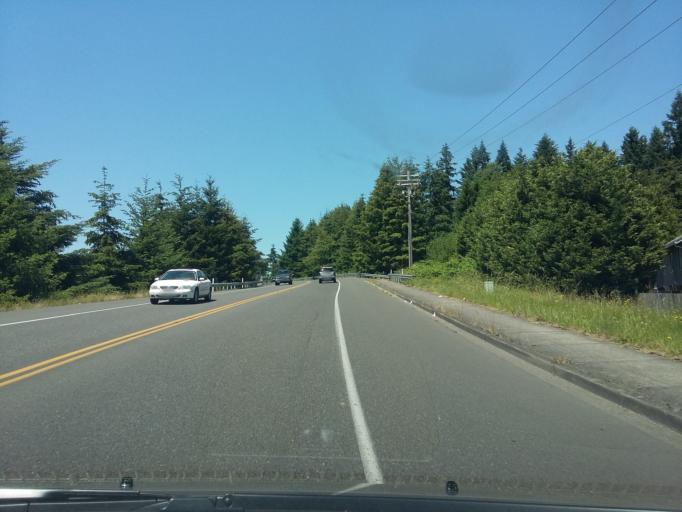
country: US
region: Washington
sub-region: Clark County
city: Five Corners
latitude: 45.6781
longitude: -122.5842
